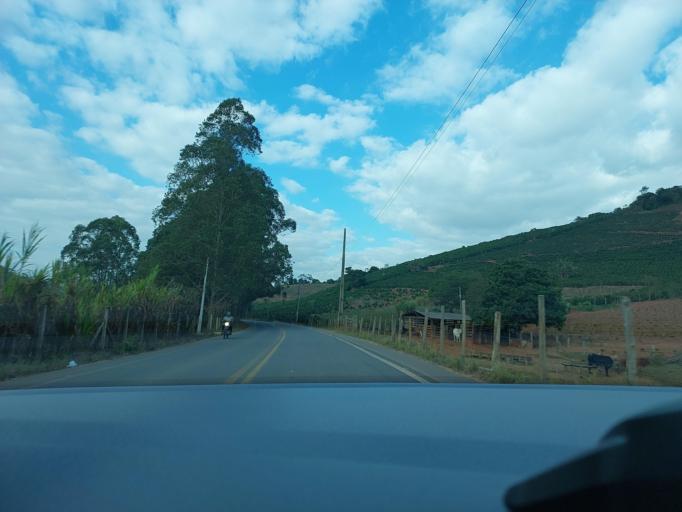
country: BR
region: Minas Gerais
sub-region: Vicosa
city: Vicosa
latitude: -20.8447
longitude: -42.6830
